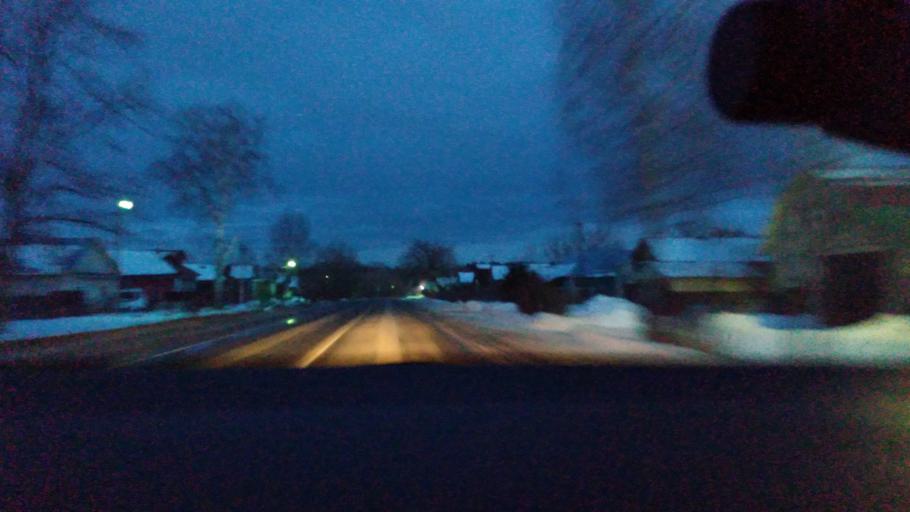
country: RU
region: Moskovskaya
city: Krasnaya Poyma
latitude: 55.1655
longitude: 39.2046
